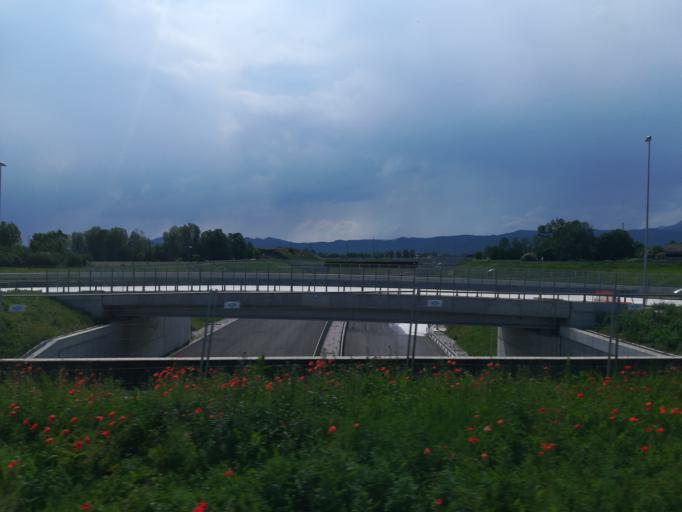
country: IT
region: Veneto
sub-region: Provincia di Vicenza
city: Novoledo
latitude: 45.6678
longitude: 11.5130
